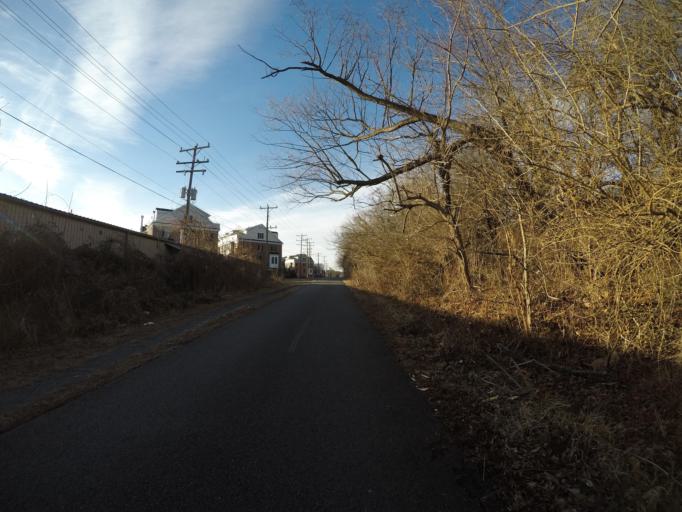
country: US
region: Virginia
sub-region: Loudoun County
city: Leesburg
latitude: 39.1086
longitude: -77.5594
